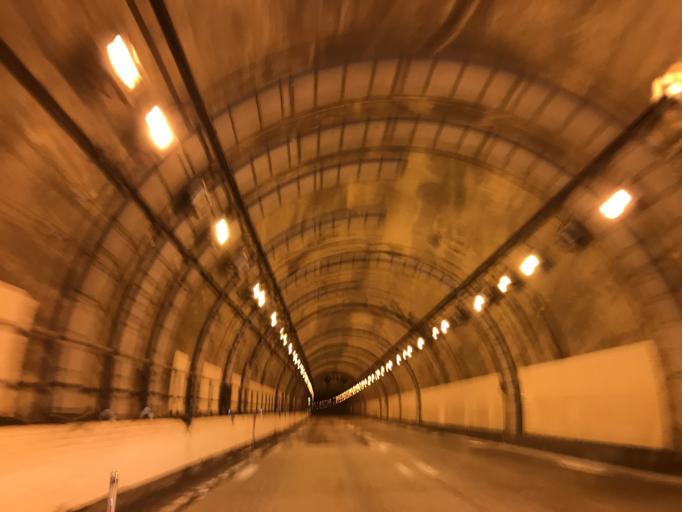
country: JP
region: Hokkaido
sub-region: Asahikawa-shi
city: Asahikawa
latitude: 43.7922
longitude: 142.2633
